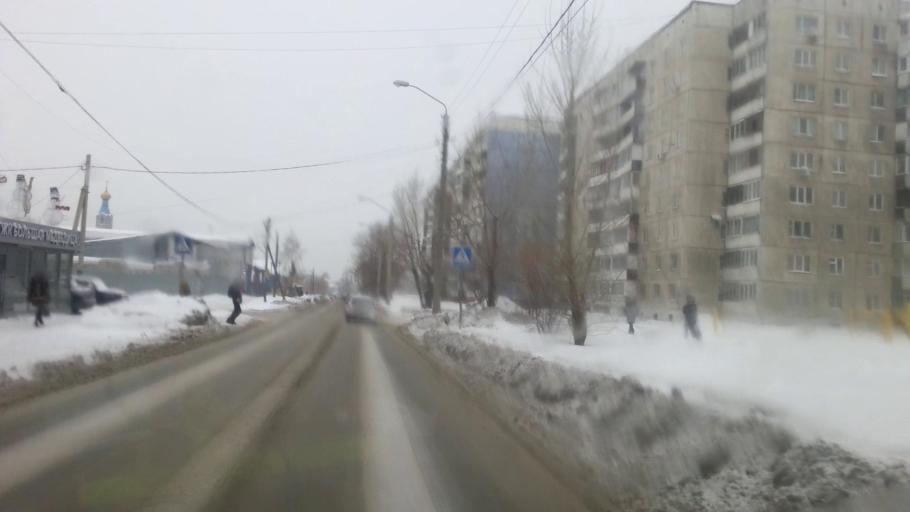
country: RU
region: Altai Krai
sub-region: Gorod Barnaulskiy
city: Barnaul
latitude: 53.3341
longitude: 83.7707
